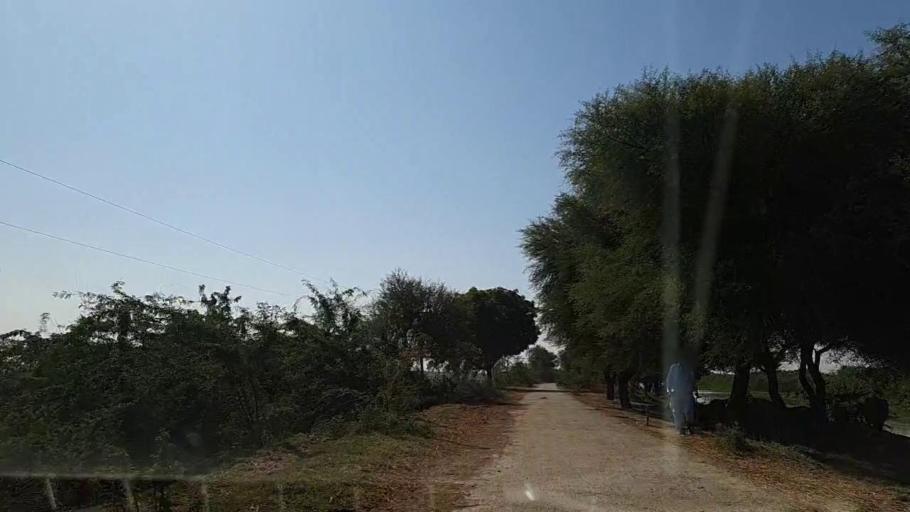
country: PK
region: Sindh
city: Chuhar Jamali
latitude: 24.5827
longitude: 68.0474
